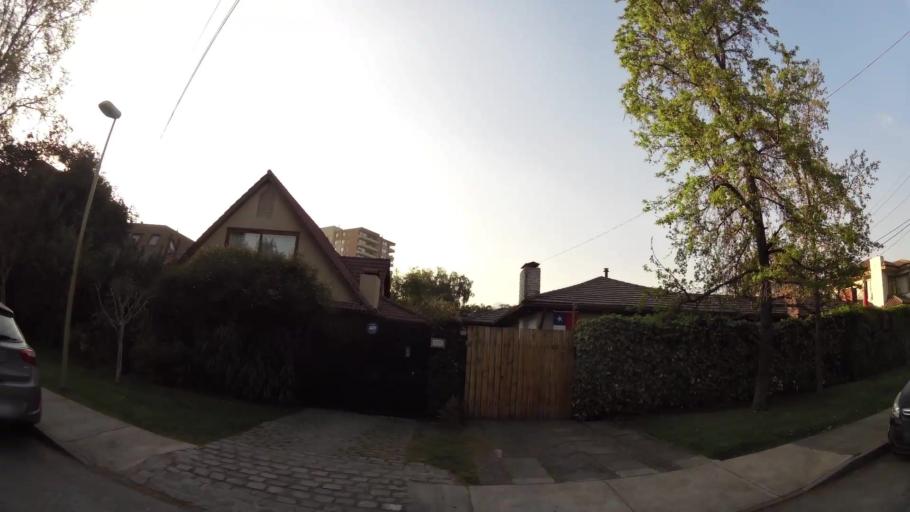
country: CL
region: Santiago Metropolitan
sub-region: Provincia de Santiago
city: Villa Presidente Frei, Nunoa, Santiago, Chile
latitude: -33.3939
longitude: -70.5531
